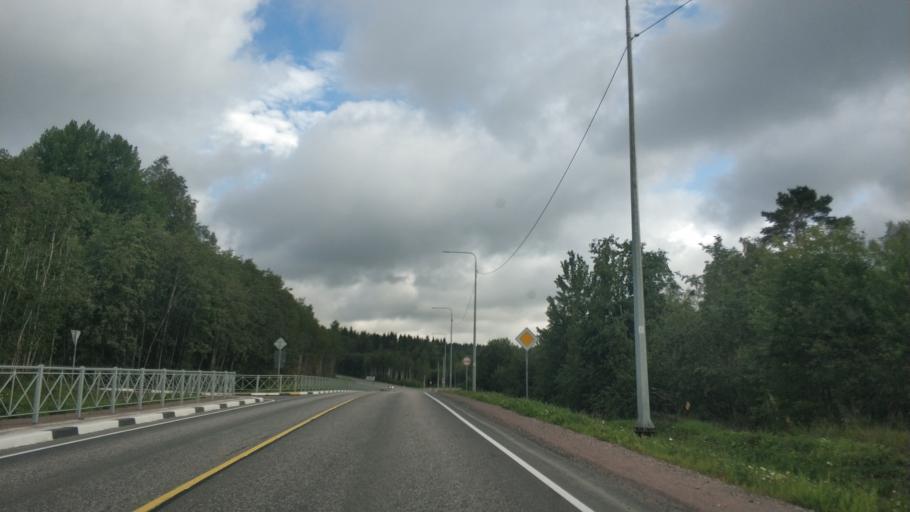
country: RU
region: Republic of Karelia
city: Khelyulya
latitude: 61.8222
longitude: 30.6344
